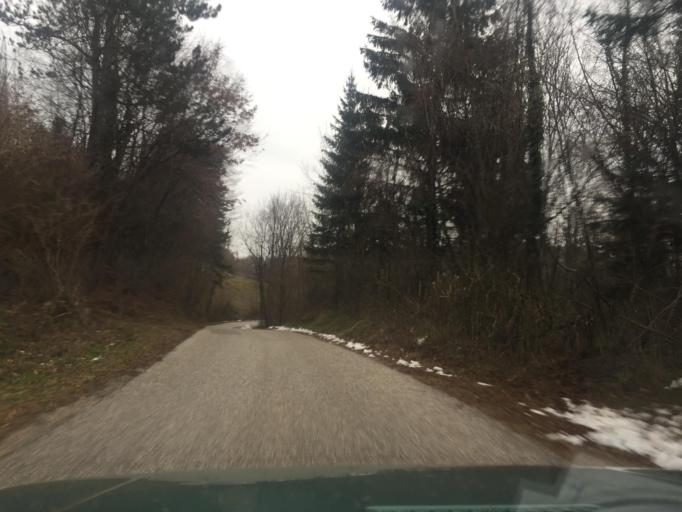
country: SI
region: Kanal
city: Kanal
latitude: 46.0674
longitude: 13.6631
